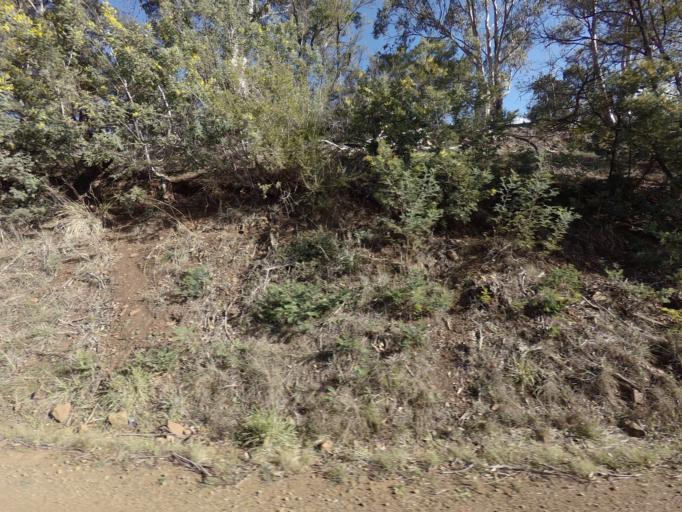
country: AU
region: Tasmania
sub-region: Derwent Valley
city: New Norfolk
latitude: -42.7034
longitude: 147.0021
